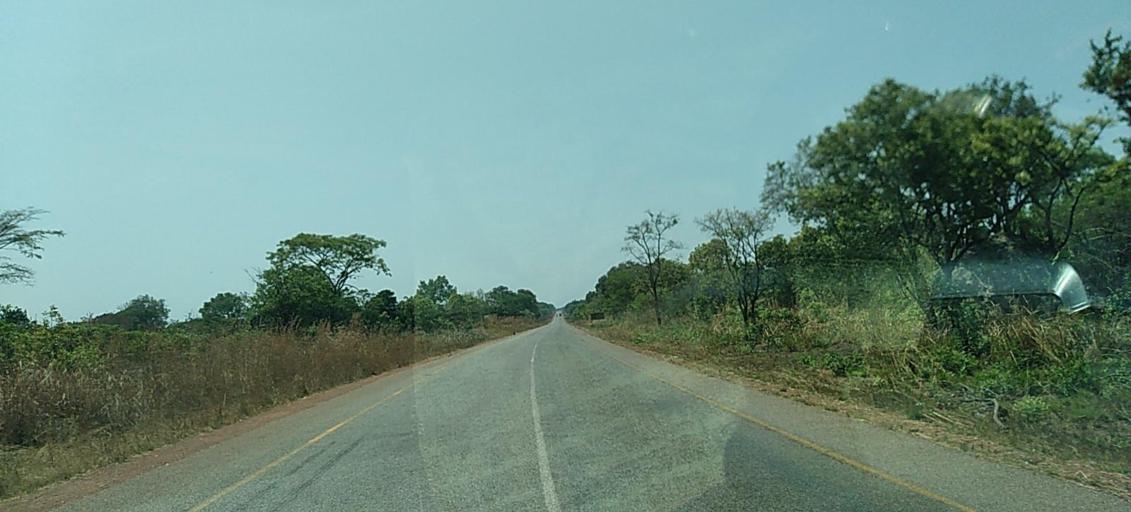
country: ZM
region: North-Western
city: Solwezi
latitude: -12.3800
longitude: 26.1905
